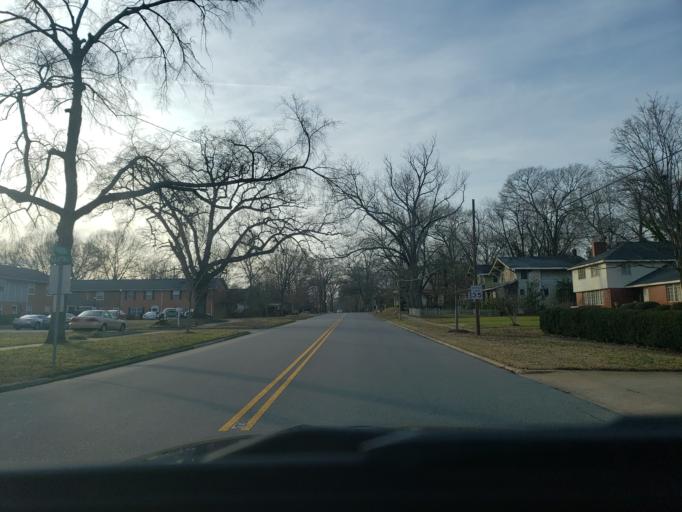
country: US
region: North Carolina
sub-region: Cleveland County
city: Shelby
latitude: 35.2912
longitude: -81.5467
